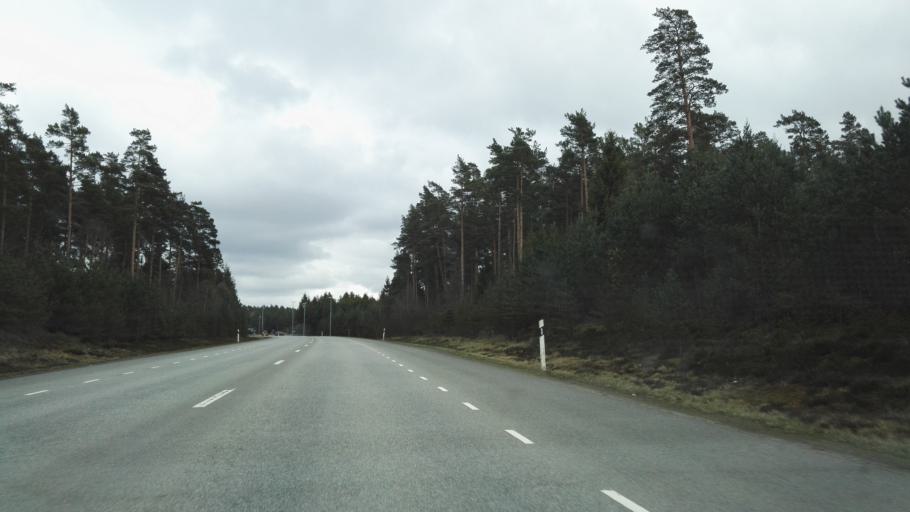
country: SE
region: Skane
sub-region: Hassleholms Kommun
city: Hassleholm
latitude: 56.1701
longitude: 13.8292
